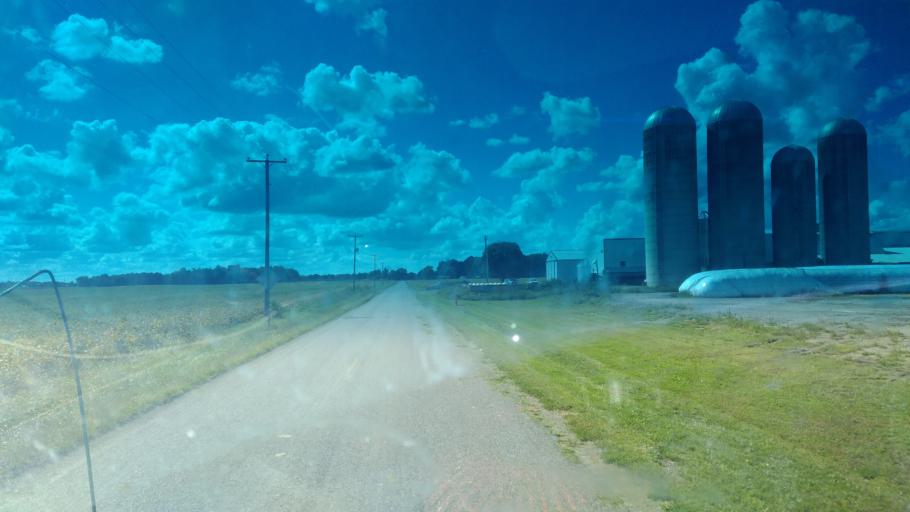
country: US
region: Ohio
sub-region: Hardin County
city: Kenton
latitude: 40.5189
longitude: -83.5425
